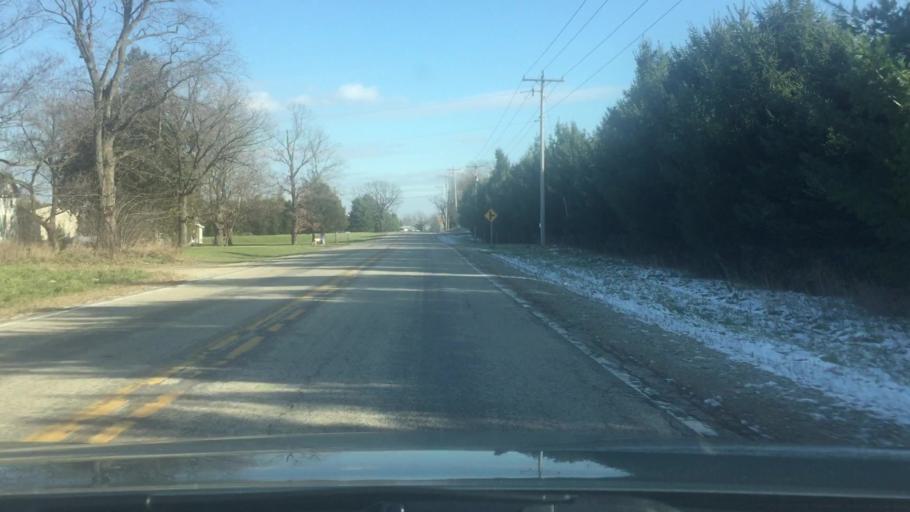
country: US
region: Wisconsin
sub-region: Jefferson County
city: Palmyra
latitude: 42.9321
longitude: -88.5749
